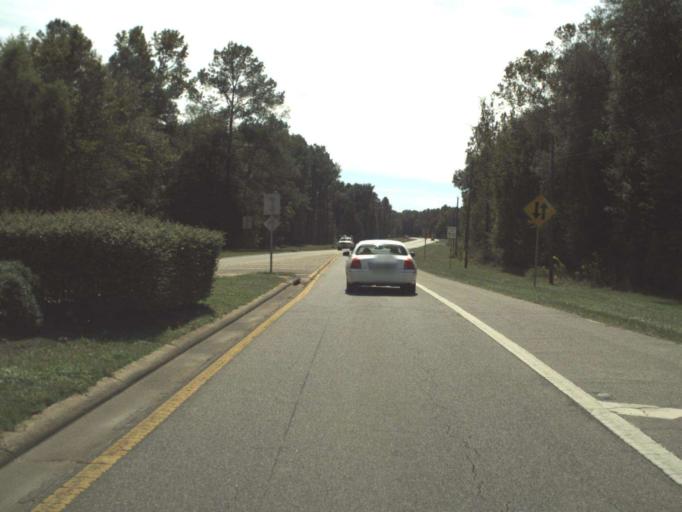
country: US
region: Florida
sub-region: Washington County
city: Chipley
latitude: 30.7412
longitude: -85.5537
